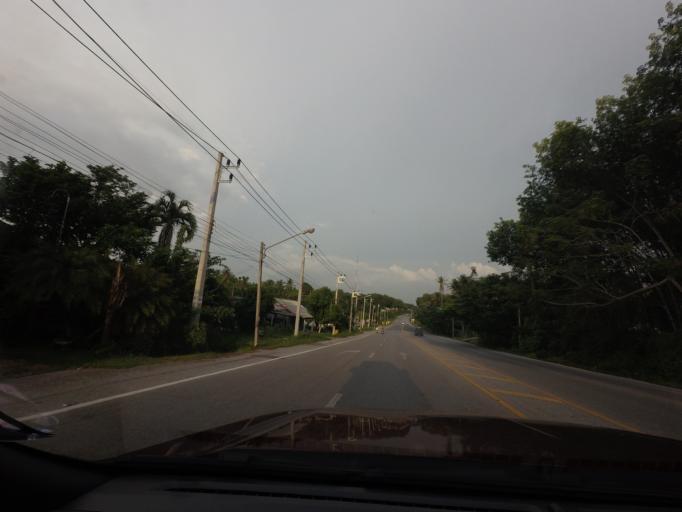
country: TH
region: Pattani
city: Khok Pho
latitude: 6.6747
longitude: 101.1522
